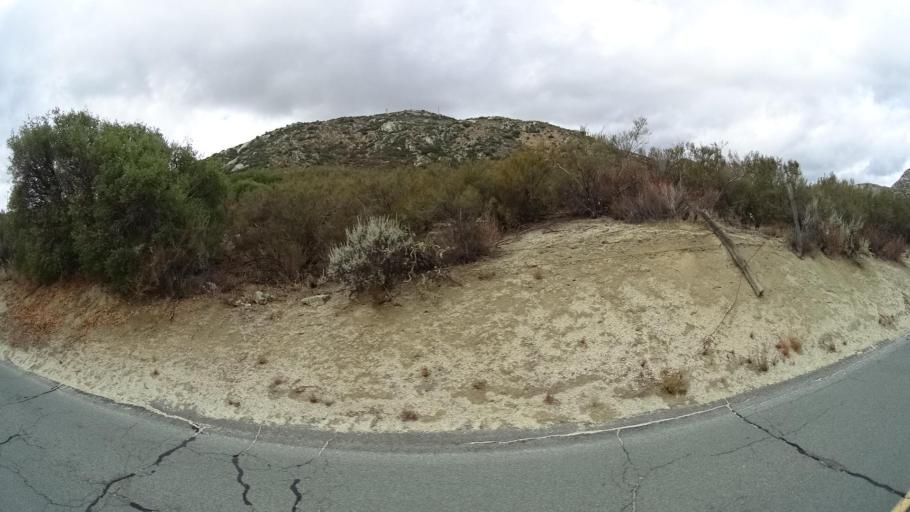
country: US
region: California
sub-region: San Diego County
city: Campo
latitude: 32.6811
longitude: -116.4299
